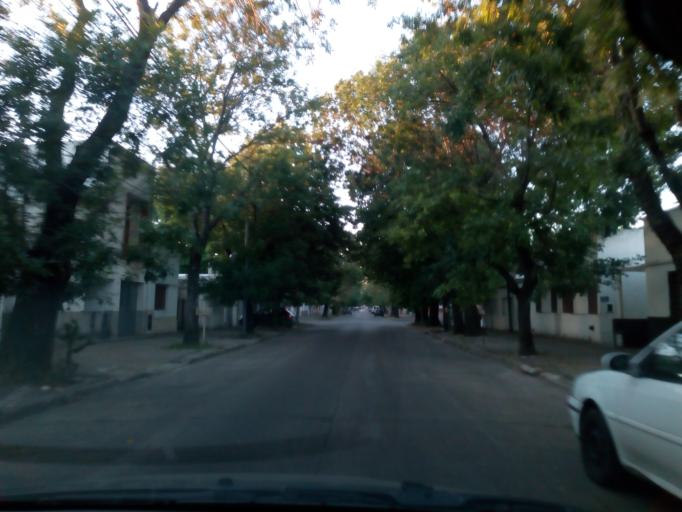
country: AR
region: Buenos Aires
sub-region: Partido de La Plata
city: La Plata
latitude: -34.9314
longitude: -57.9595
